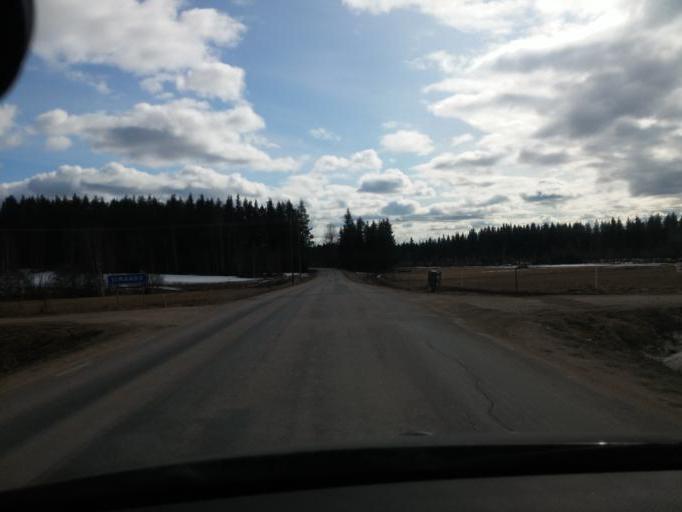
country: SE
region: Gaevleborg
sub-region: Ljusdals Kommun
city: Ljusdal
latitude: 61.8142
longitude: 16.1498
